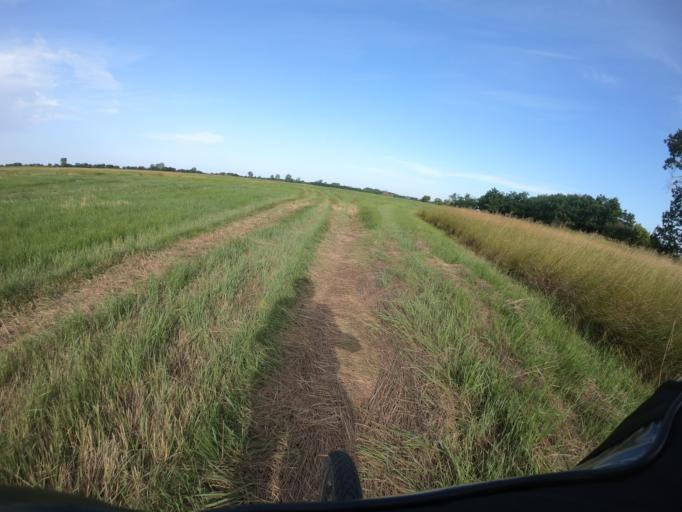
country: HU
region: Hajdu-Bihar
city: Tiszacsege
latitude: 47.6135
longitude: 21.0243
